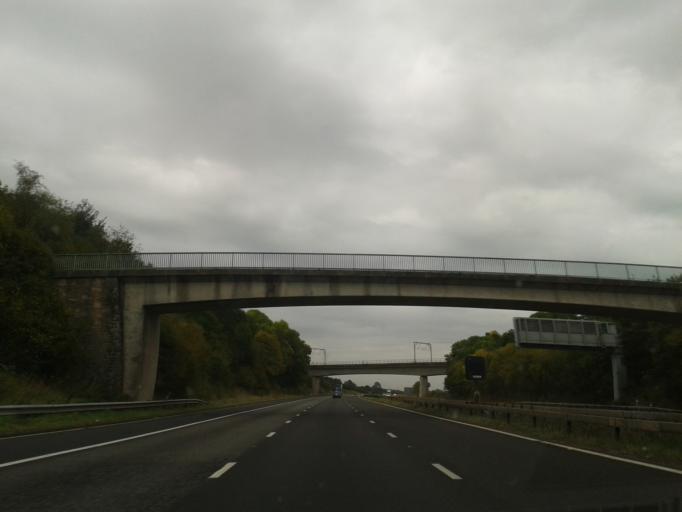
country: GB
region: England
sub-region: Cumbria
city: Penrith
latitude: 54.6369
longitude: -2.7298
